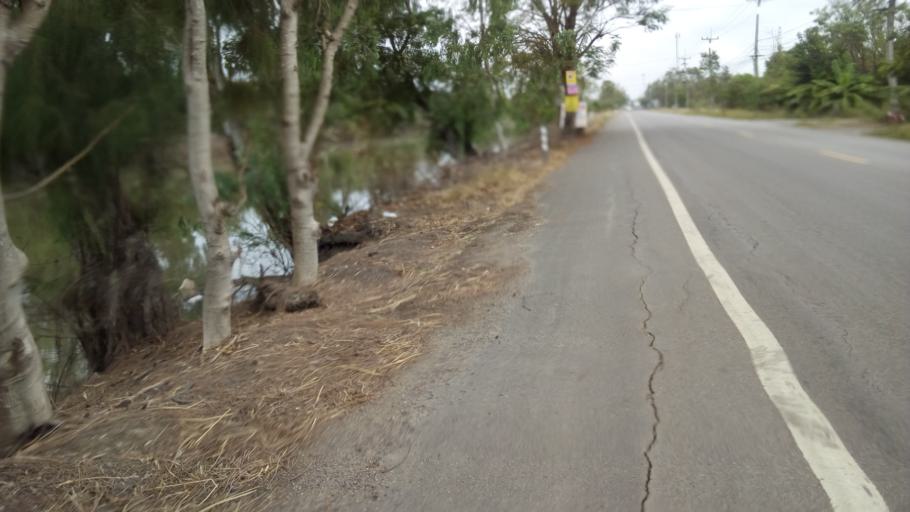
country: TH
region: Pathum Thani
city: Nong Suea
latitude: 14.2092
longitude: 100.8234
